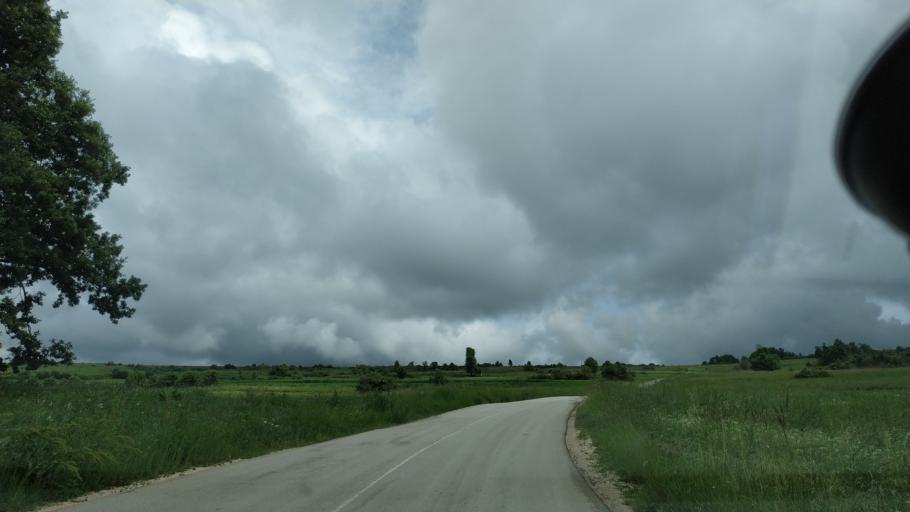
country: RS
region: Central Serbia
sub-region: Zajecarski Okrug
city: Soko Banja
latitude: 43.6902
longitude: 21.9318
